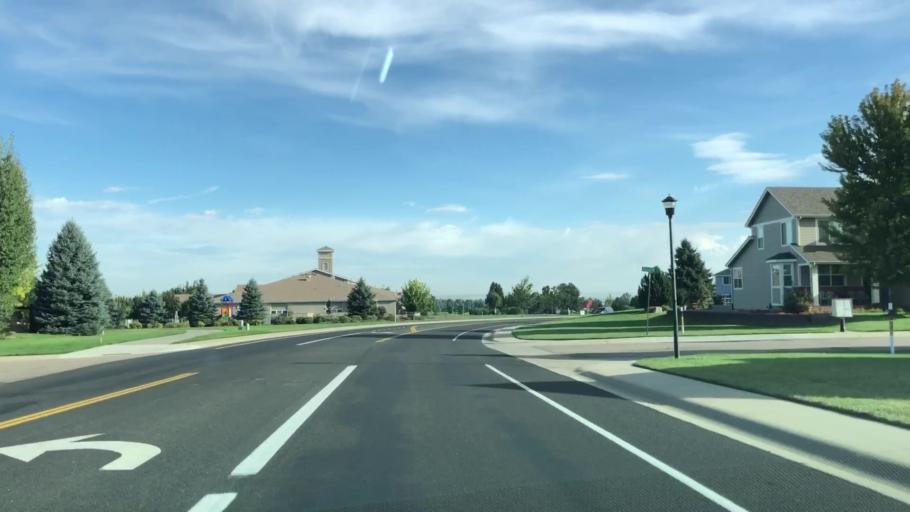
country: US
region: Colorado
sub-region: Weld County
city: Windsor
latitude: 40.4723
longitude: -104.9794
